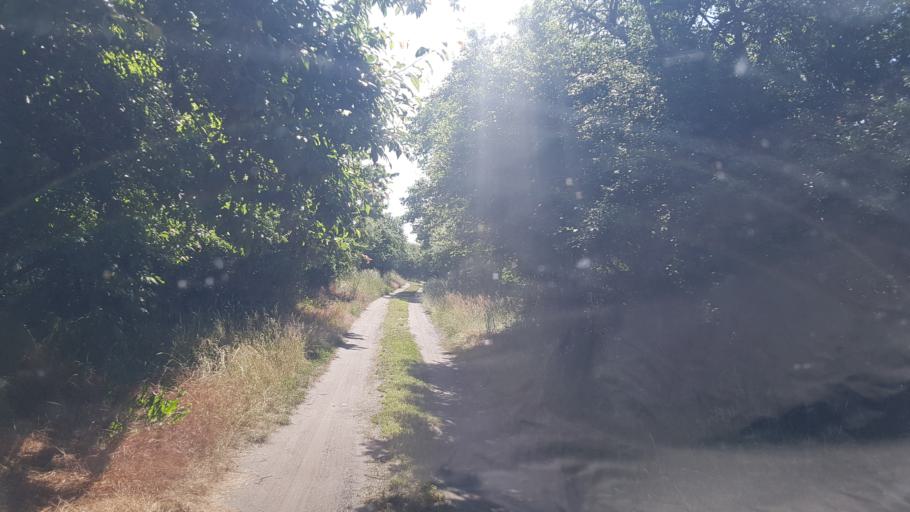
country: DE
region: Brandenburg
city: Plessa
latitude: 51.4693
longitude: 13.6004
